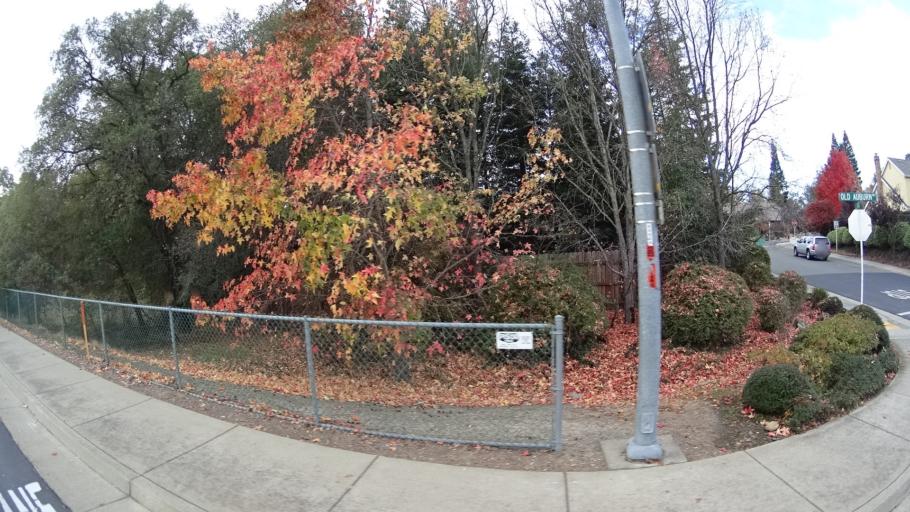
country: US
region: California
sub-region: Sacramento County
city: Citrus Heights
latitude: 38.7207
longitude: -121.2445
